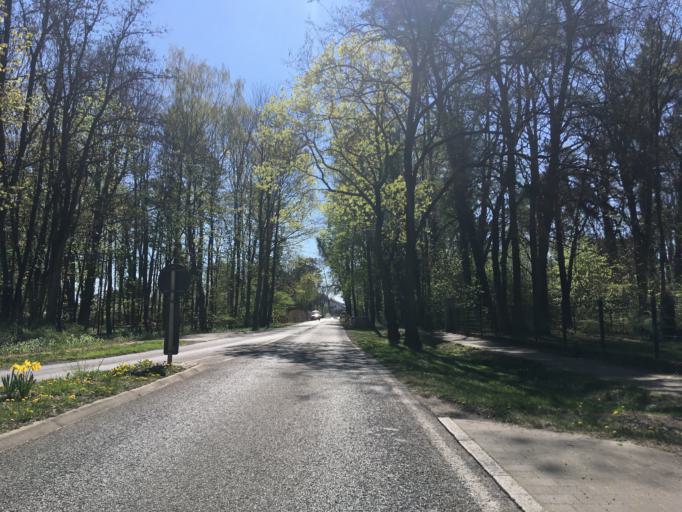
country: DE
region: Brandenburg
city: Bernau bei Berlin
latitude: 52.7085
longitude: 13.5843
